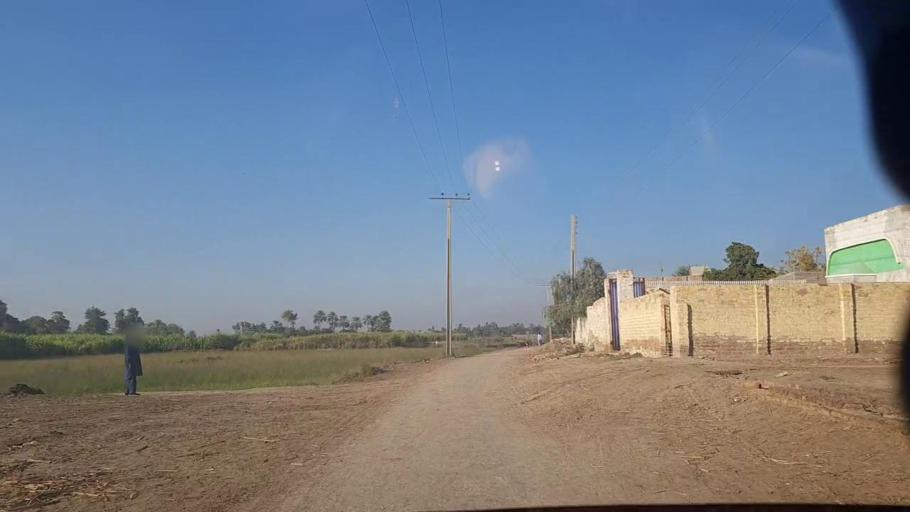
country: PK
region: Sindh
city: Sobhadero
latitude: 27.3814
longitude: 68.4168
